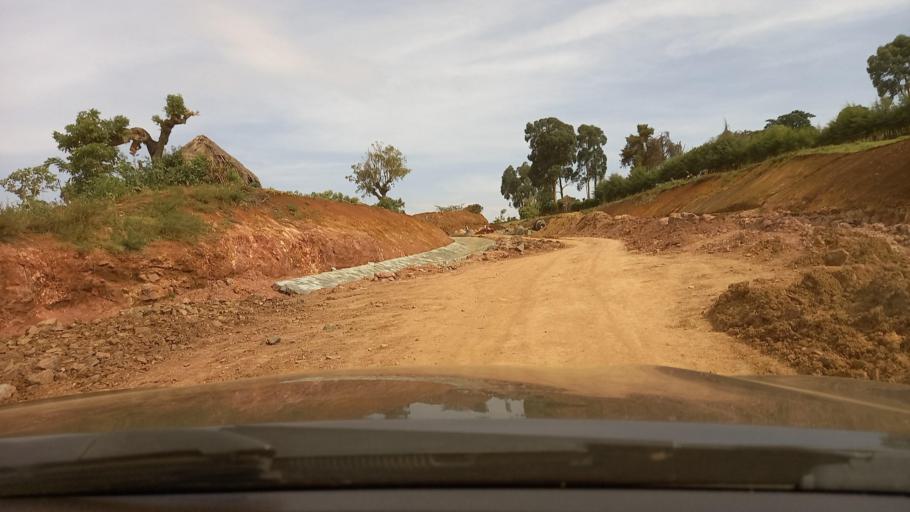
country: ET
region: Southern Nations, Nationalities, and People's Region
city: Mizan Teferi
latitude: 6.1661
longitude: 35.7383
